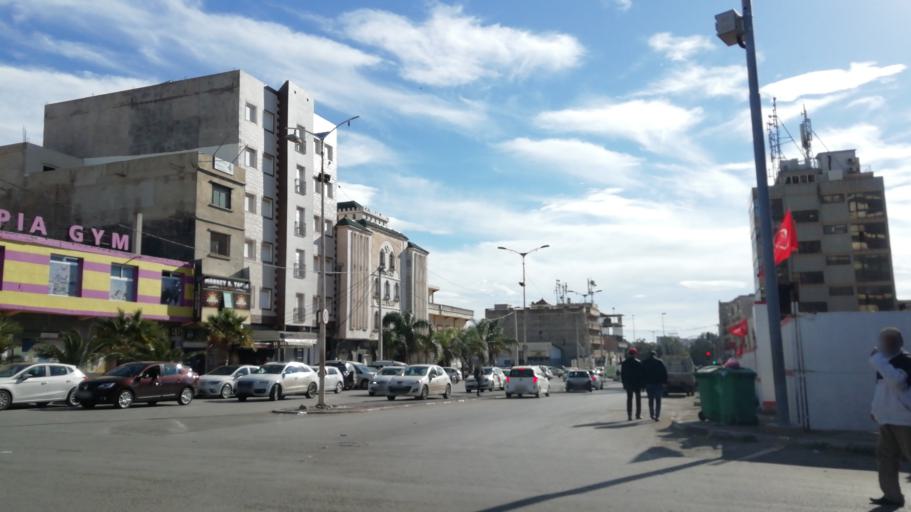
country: DZ
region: Oran
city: Oran
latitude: 35.6992
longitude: -0.6183
